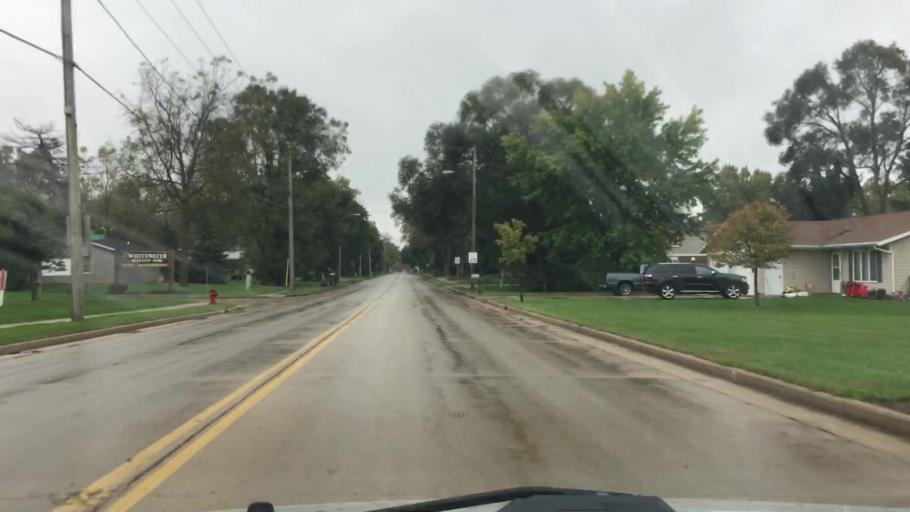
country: US
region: Wisconsin
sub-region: Walworth County
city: Whitewater
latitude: 42.8385
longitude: -88.7179
